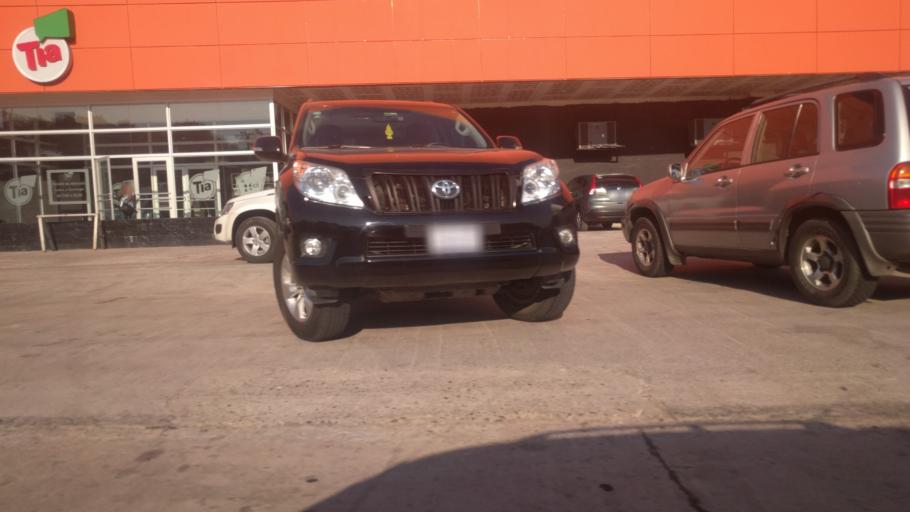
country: BO
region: Santa Cruz
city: Santa Cruz de la Sierra
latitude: -17.7550
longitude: -63.2004
